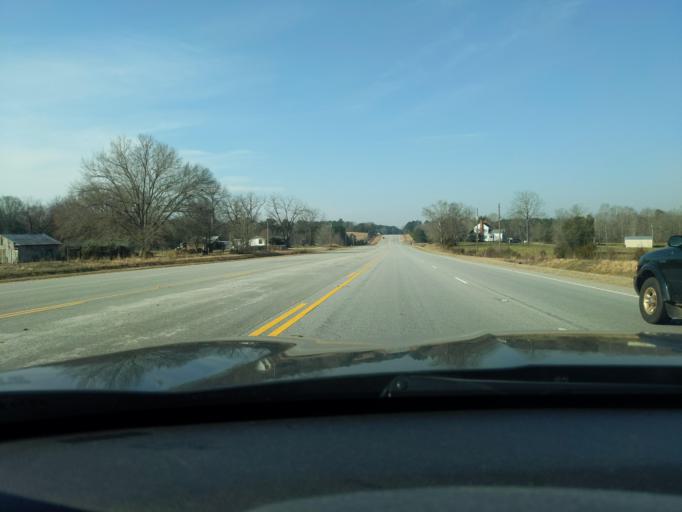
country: US
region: South Carolina
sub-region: Abbeville County
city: Abbeville
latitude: 34.1270
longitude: -82.4351
